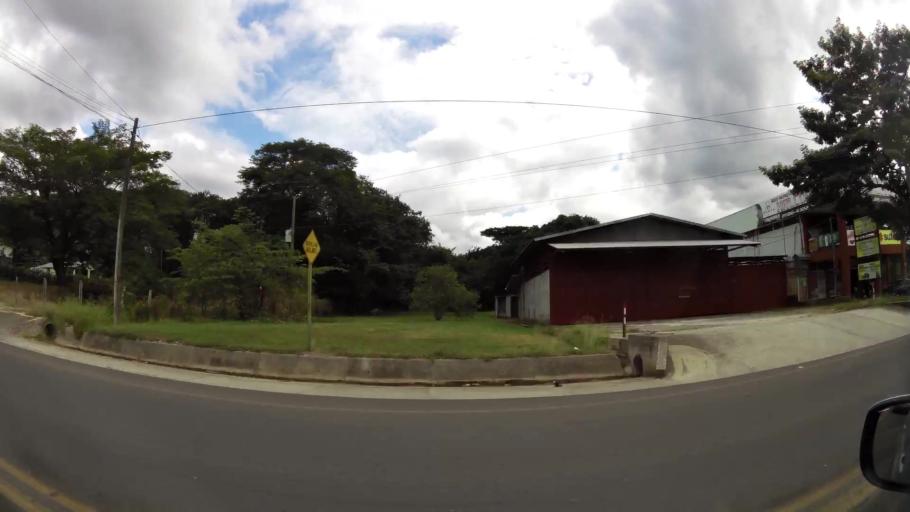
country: CR
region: Guanacaste
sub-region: Canton de Nicoya
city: Nicoya
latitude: 10.1575
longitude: -85.4489
